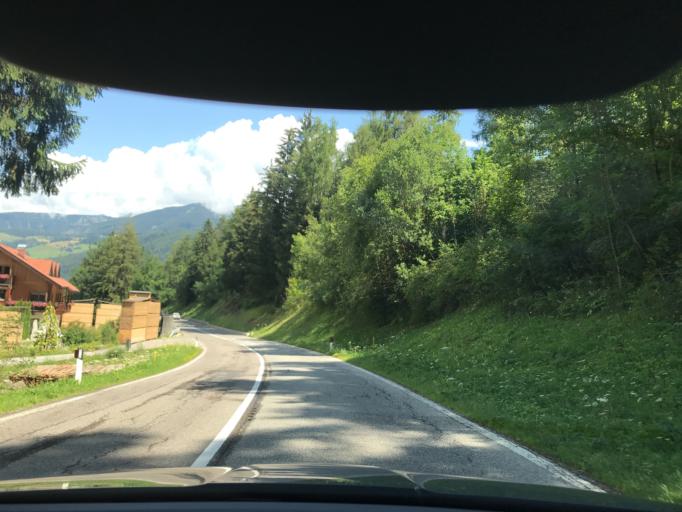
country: IT
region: Trentino-Alto Adige
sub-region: Bolzano
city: Valdaora di Mezzo
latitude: 46.7556
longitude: 12.0210
